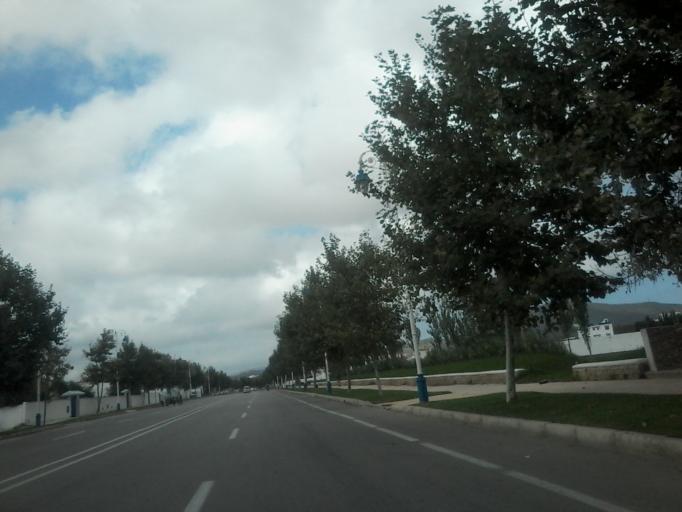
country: MA
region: Tanger-Tetouan
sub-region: Tetouan
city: Martil
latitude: 35.6386
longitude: -5.2904
